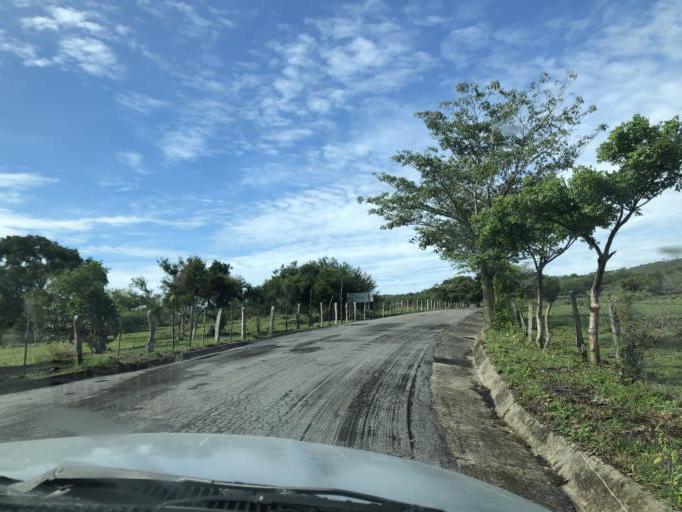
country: MX
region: Veracruz
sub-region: Alto Lucero de Gutierrez Barrios
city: Palma Sola
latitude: 19.8032
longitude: -96.5429
